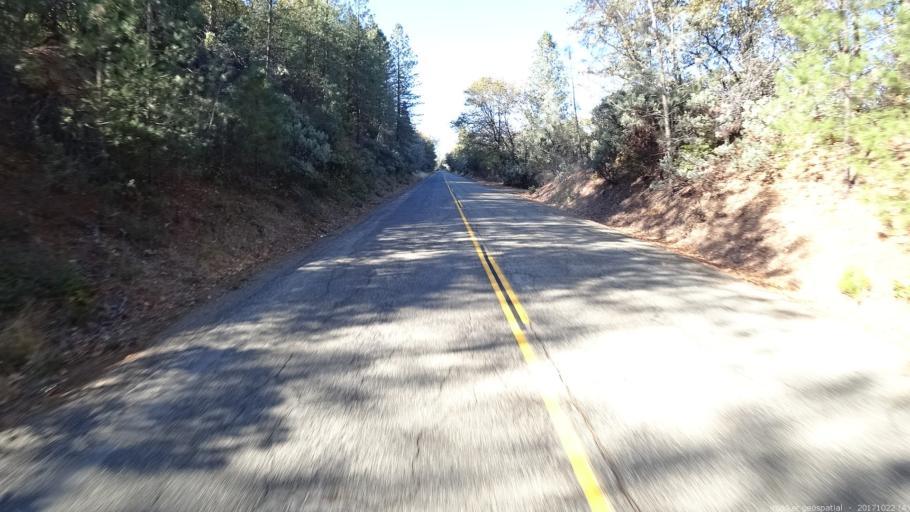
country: US
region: California
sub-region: Shasta County
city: Shasta Lake
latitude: 40.8594
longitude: -122.3551
